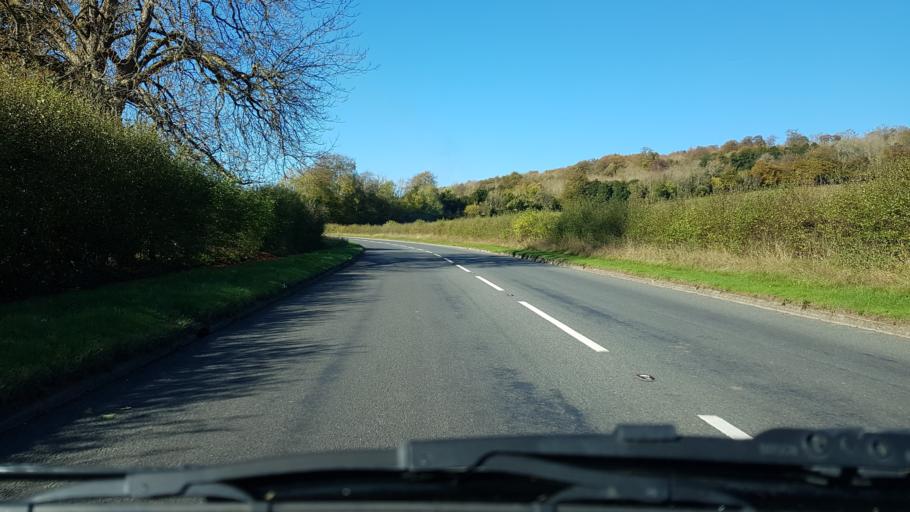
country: GB
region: England
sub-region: Surrey
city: East Horsley
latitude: 51.2222
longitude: -0.4618
